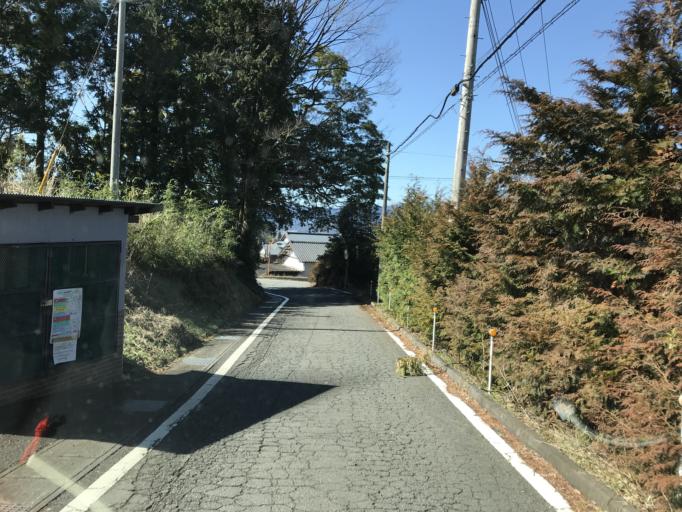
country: JP
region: Shizuoka
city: Fujinomiya
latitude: 35.2451
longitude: 138.6602
